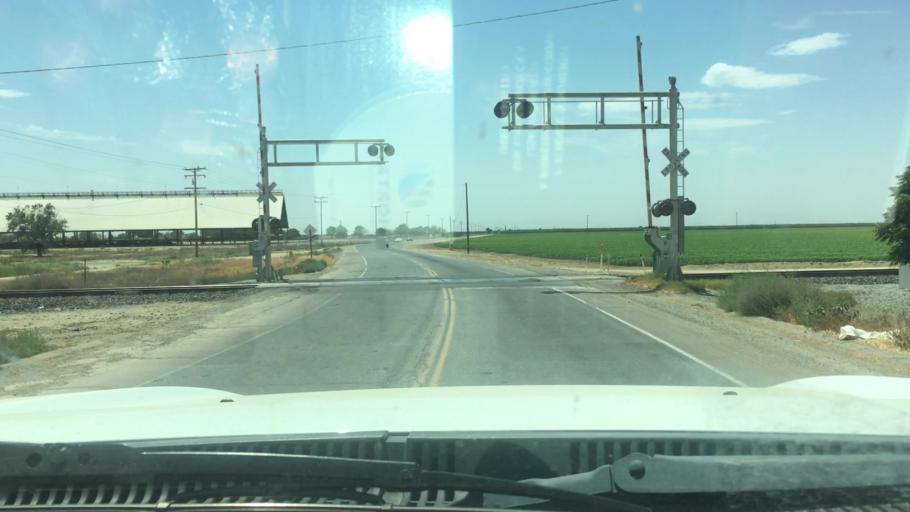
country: US
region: California
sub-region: Tulare County
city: Tipton
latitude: 36.0661
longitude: -119.3159
